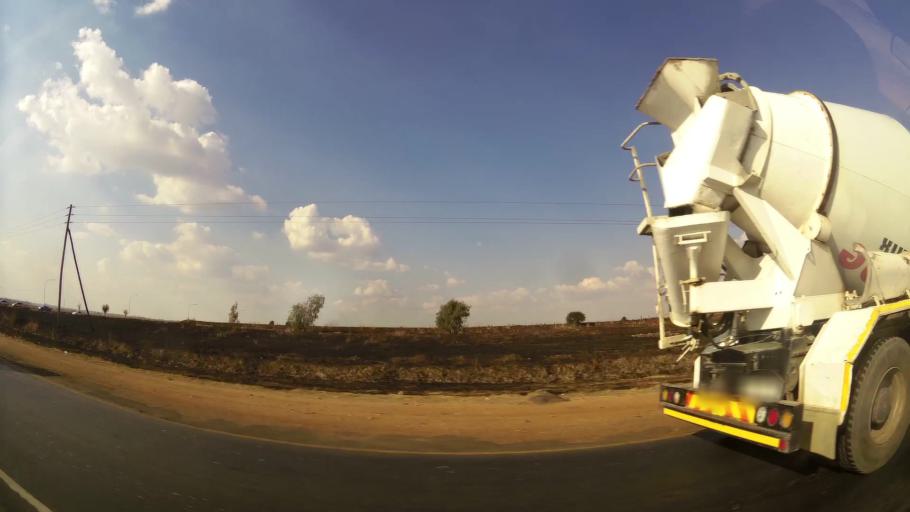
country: ZA
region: Gauteng
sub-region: Ekurhuleni Metropolitan Municipality
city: Brakpan
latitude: -26.3406
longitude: 28.3412
